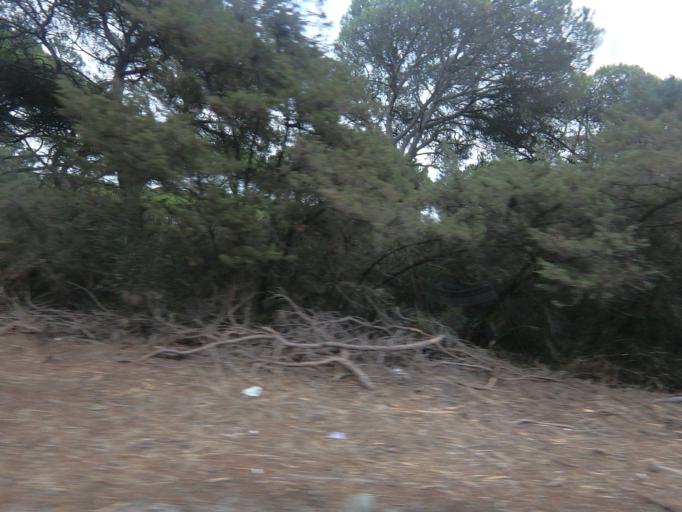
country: PT
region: Setubal
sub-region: Almada
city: Charneca
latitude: 38.5838
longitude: -9.1941
